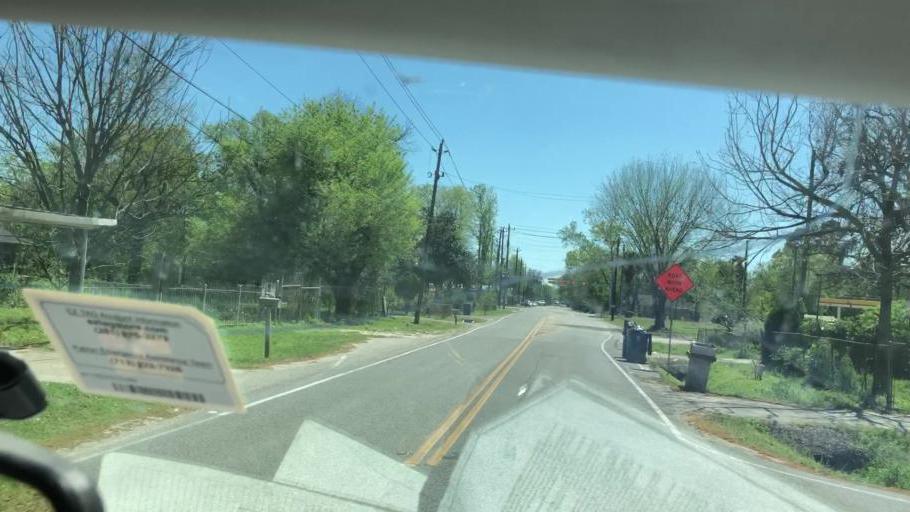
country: US
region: Texas
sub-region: Harris County
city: Aldine
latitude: 29.9035
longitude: -95.3910
